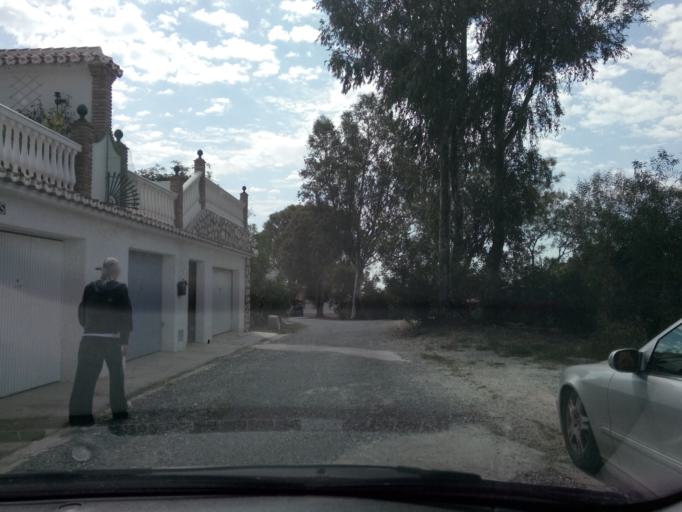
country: ES
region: Andalusia
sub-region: Provincia de Malaga
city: Mijas
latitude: 36.5739
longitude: -4.6078
